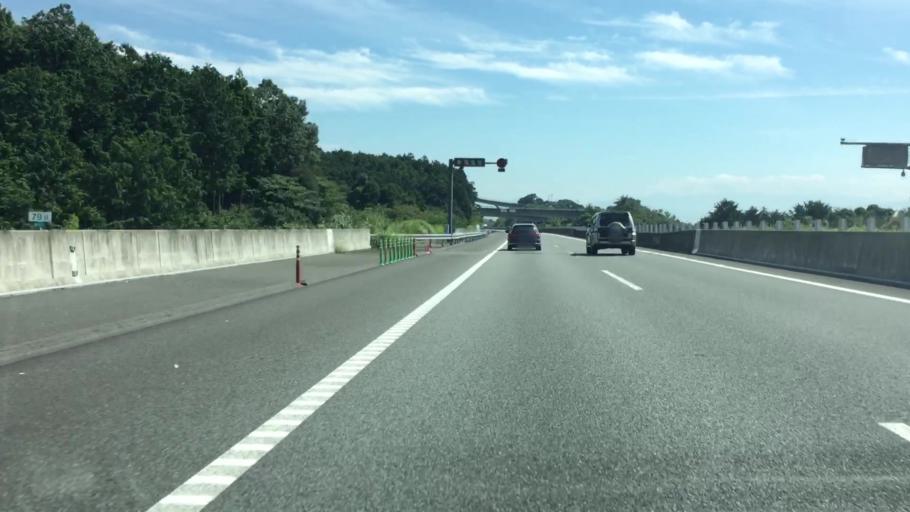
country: JP
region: Shizuoka
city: Fuji
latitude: 35.1810
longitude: 138.7303
